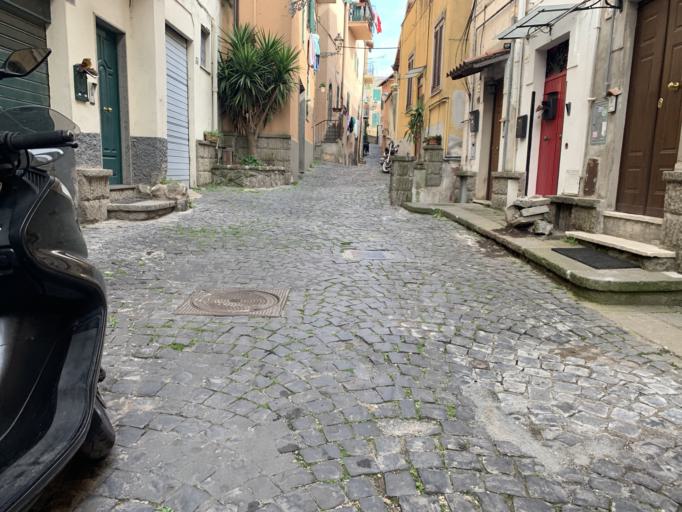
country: IT
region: Latium
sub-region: Citta metropolitana di Roma Capitale
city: Castel Gandolfo
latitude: 41.7688
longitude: 12.6597
